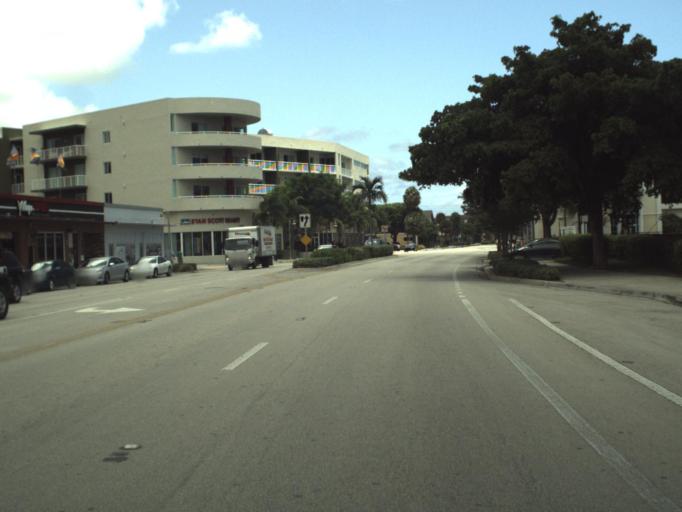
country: US
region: Florida
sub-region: Broward County
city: Wilton Manors
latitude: 26.1567
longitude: -80.1378
